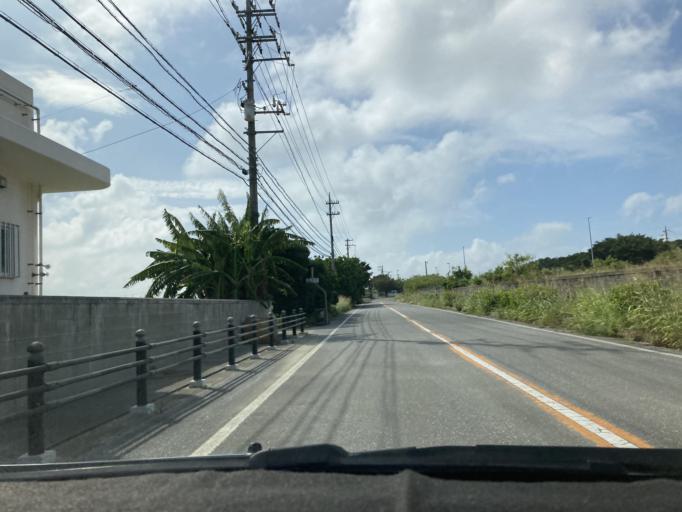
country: JP
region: Okinawa
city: Itoman
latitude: 26.0940
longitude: 127.7173
